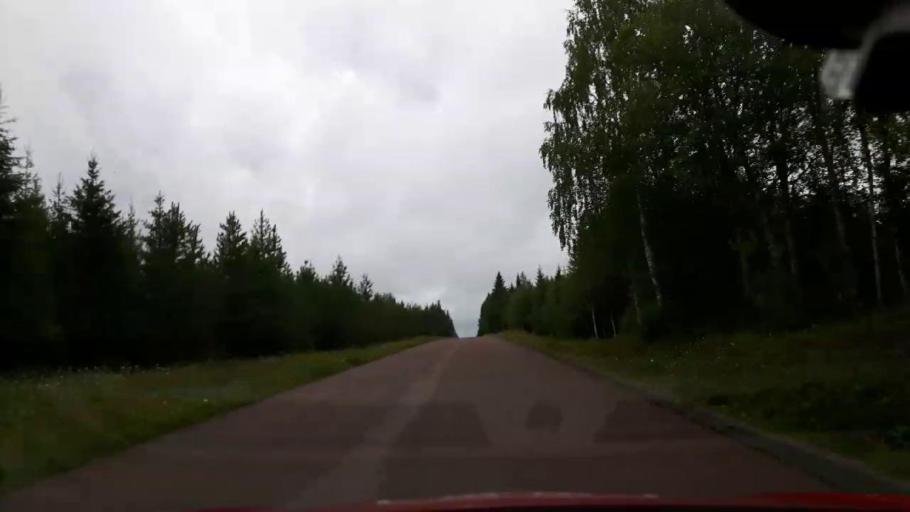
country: SE
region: Jaemtland
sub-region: Krokoms Kommun
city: Valla
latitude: 63.3681
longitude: 13.7481
